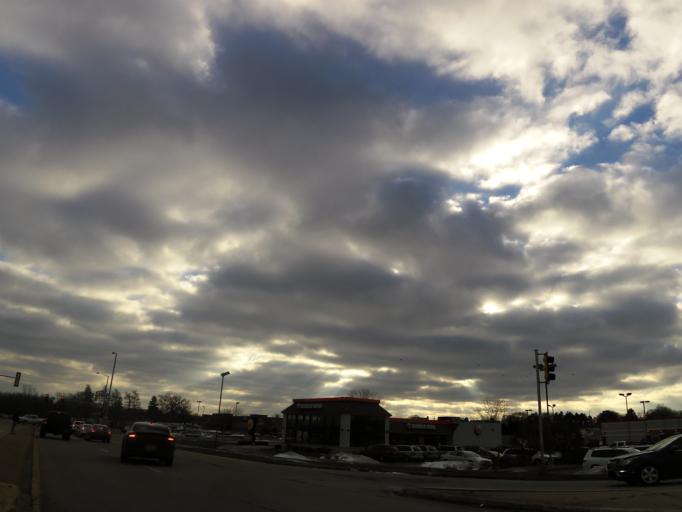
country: US
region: Illinois
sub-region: Winnebago County
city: Cherry Valley
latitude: 42.2421
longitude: -88.9756
